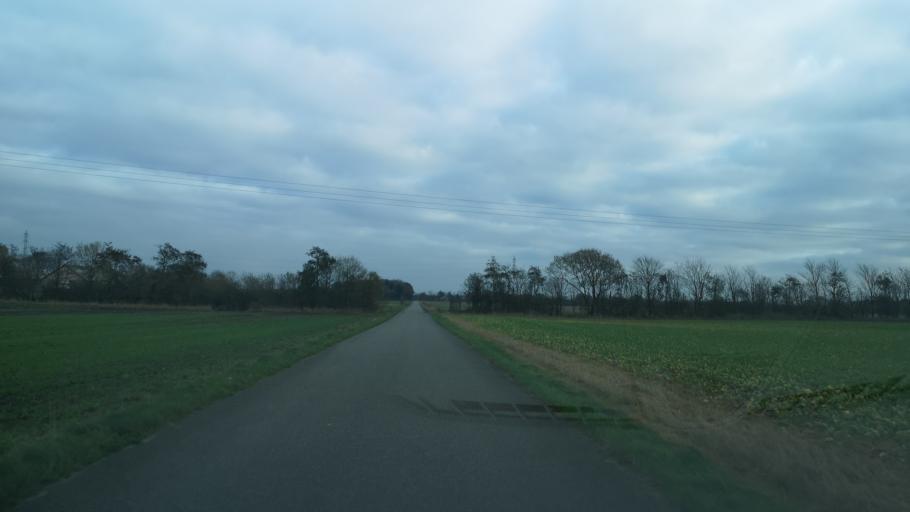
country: DK
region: Central Jutland
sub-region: Ringkobing-Skjern Kommune
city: Videbaek
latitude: 56.0357
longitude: 8.5844
